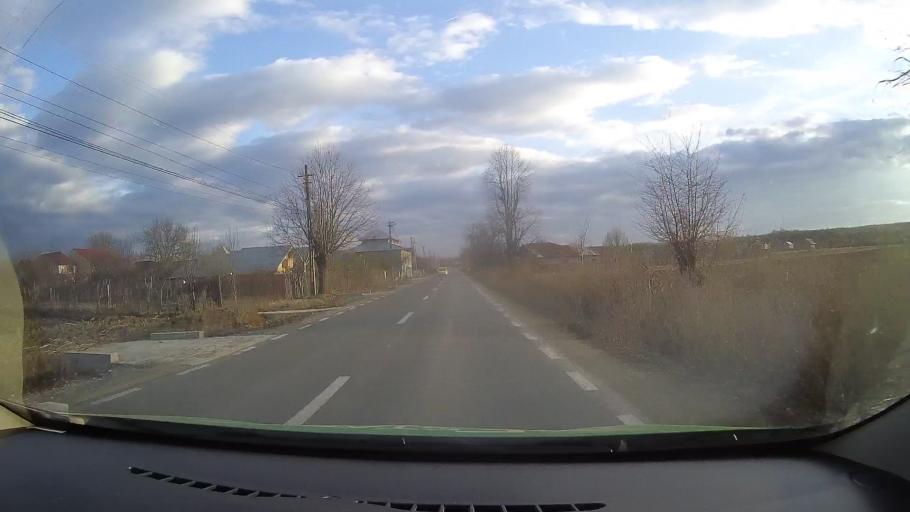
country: RO
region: Dambovita
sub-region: Comuna I. L. Caragiale
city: Ghirdoveni
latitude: 44.9568
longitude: 25.6576
